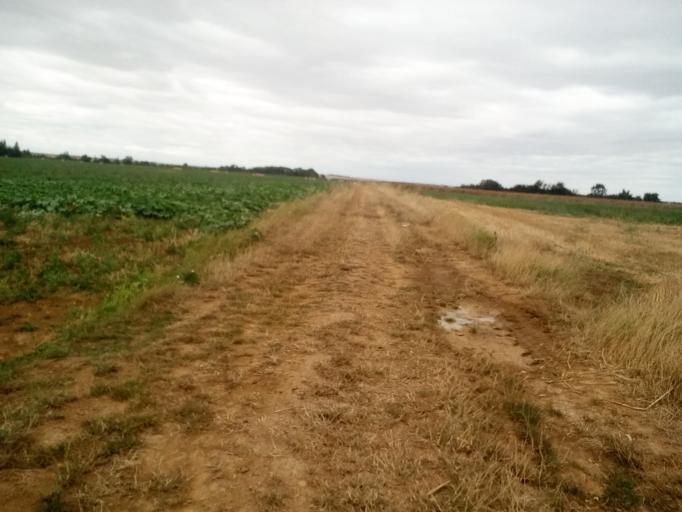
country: FR
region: Lower Normandy
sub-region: Departement du Calvados
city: Clinchamps-sur-Orne
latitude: 49.0575
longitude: -0.4117
